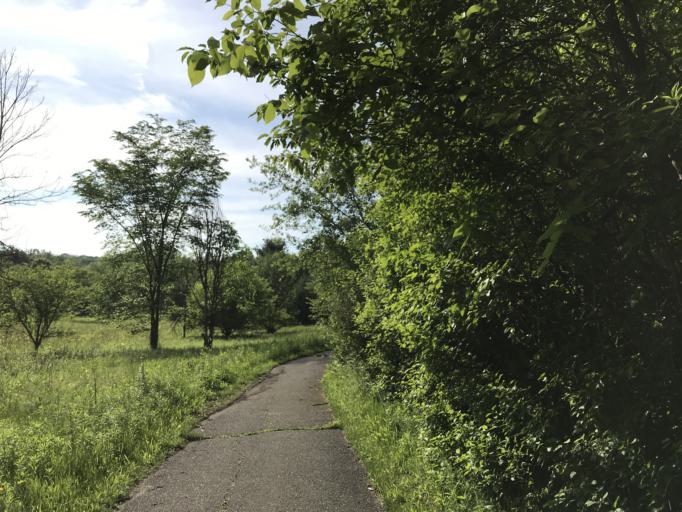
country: US
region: Michigan
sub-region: Oakland County
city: Farmington Hills
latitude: 42.4755
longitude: -83.3822
